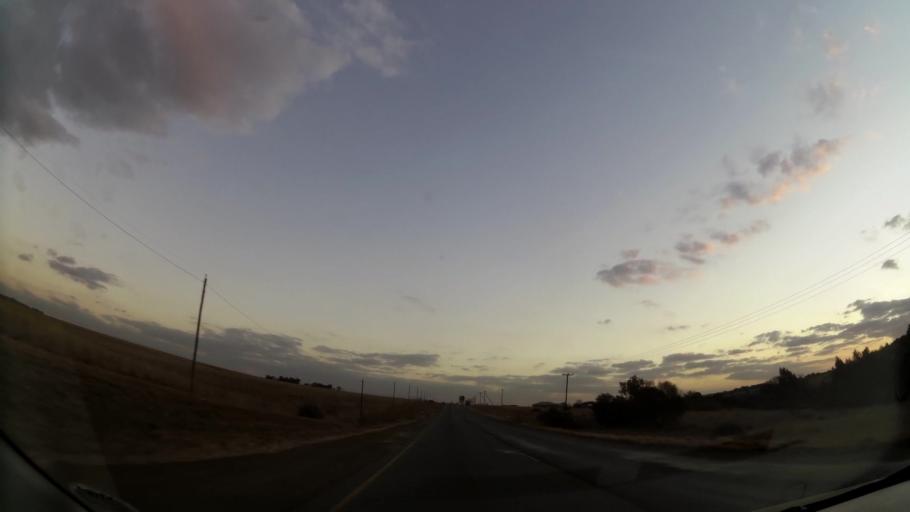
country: ZA
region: Gauteng
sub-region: West Rand District Municipality
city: Krugersdorp
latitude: -26.0522
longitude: 27.7103
